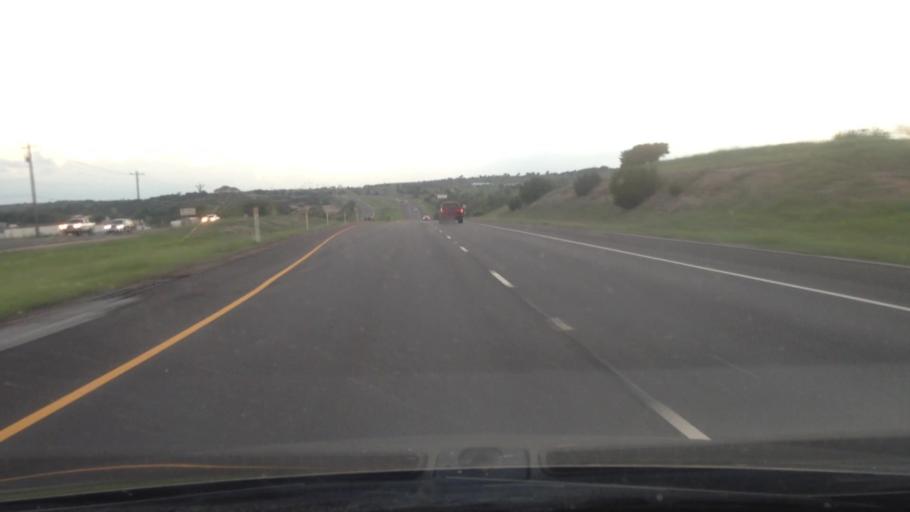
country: US
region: Texas
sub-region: Hood County
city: DeCordova
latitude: 32.5103
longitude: -97.6375
